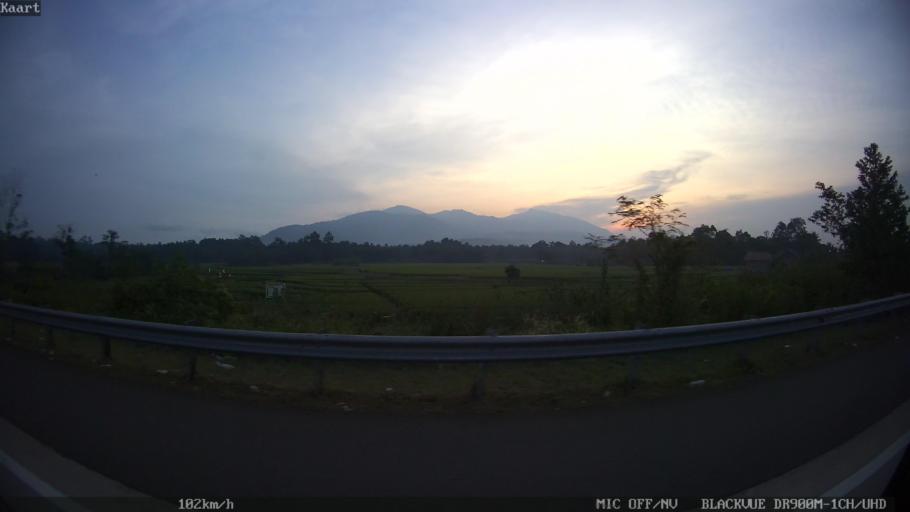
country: ID
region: Lampung
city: Penengahan
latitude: -5.7632
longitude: 105.7132
